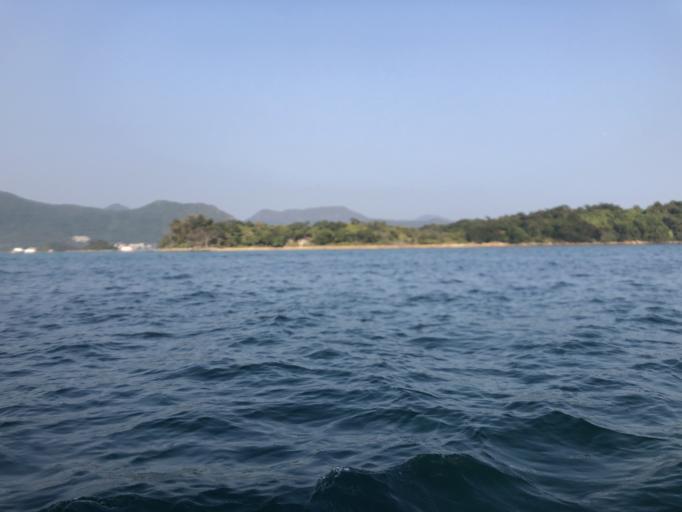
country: HK
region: Sai Kung
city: Sai Kung
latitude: 22.3792
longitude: 114.2771
